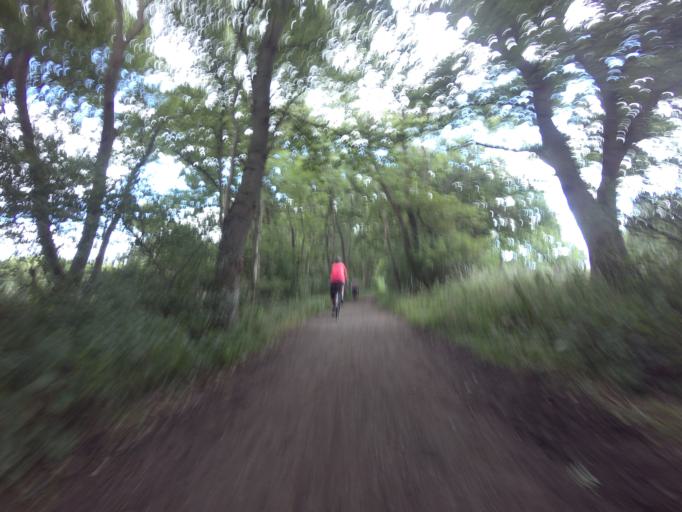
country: GB
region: England
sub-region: East Sussex
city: Hailsham
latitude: 50.8374
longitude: 0.2231
